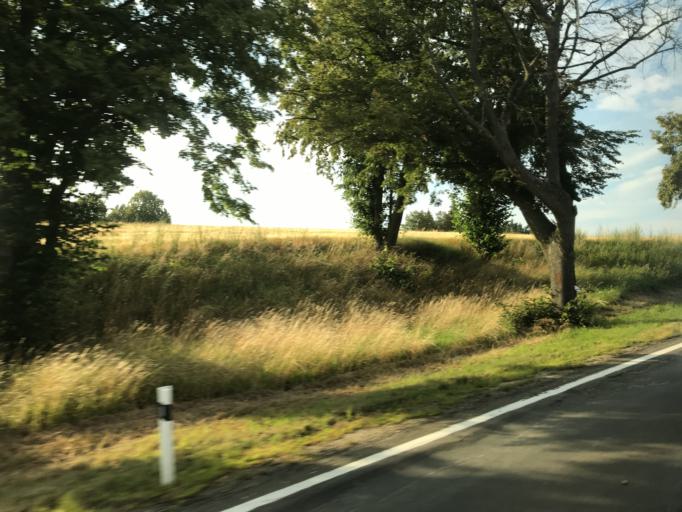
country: CZ
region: Jihocesky
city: Rudolfov
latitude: 49.0003
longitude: 14.5512
